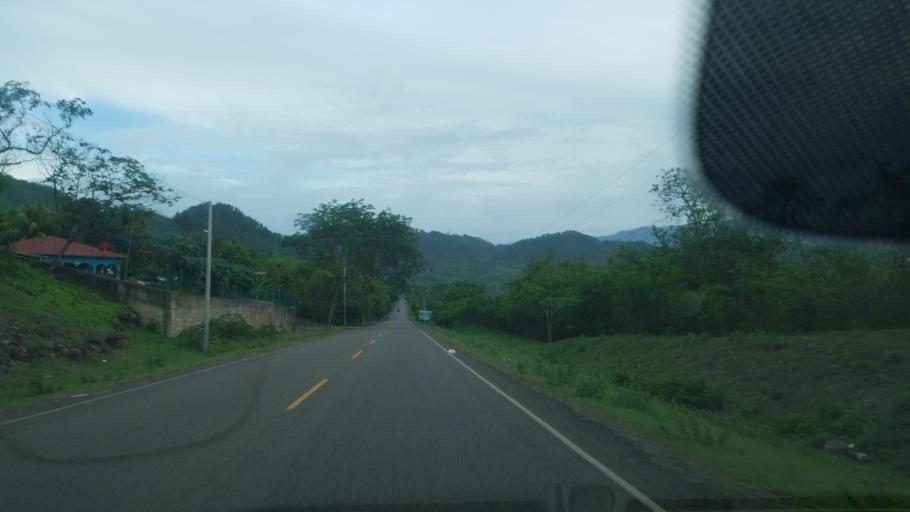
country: HN
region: Santa Barbara
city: San Vicente Centenario
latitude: 14.8667
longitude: -88.2484
